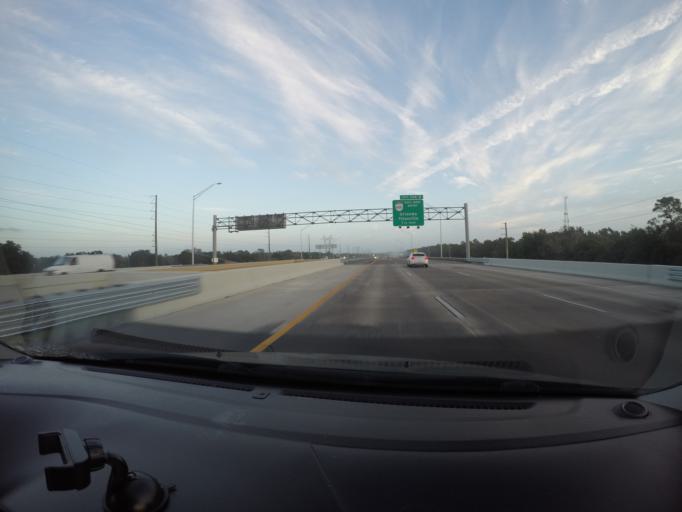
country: US
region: Florida
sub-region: Orange County
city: Azalea Park
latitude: 28.5246
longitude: -81.2507
